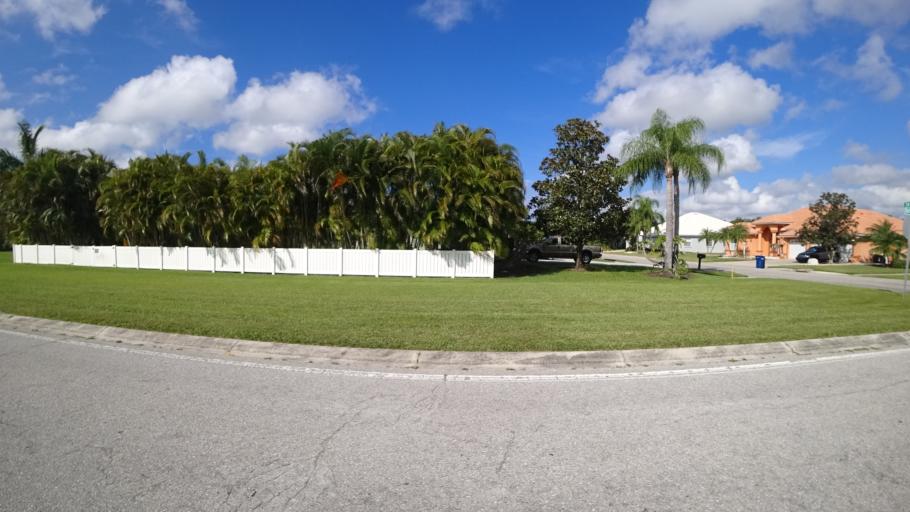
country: US
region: Florida
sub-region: Sarasota County
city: North Sarasota
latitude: 27.4077
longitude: -82.5134
